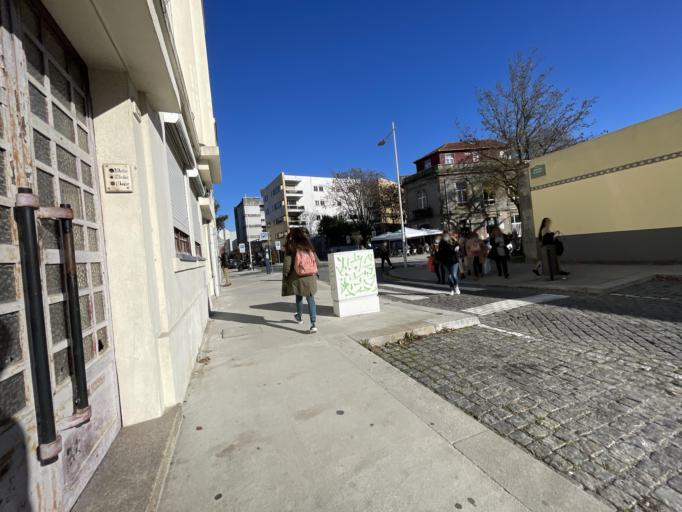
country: PT
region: Porto
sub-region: Porto
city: Porto
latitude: 41.1472
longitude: -8.6001
